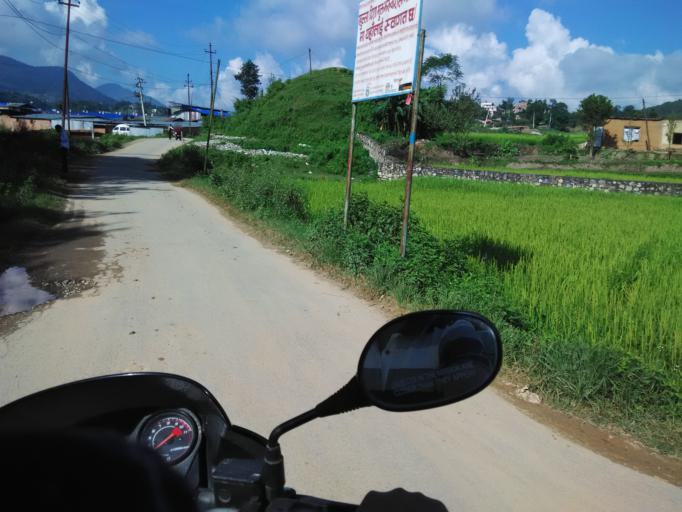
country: NP
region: Central Region
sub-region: Bagmati Zone
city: Patan
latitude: 27.6068
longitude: 85.3493
